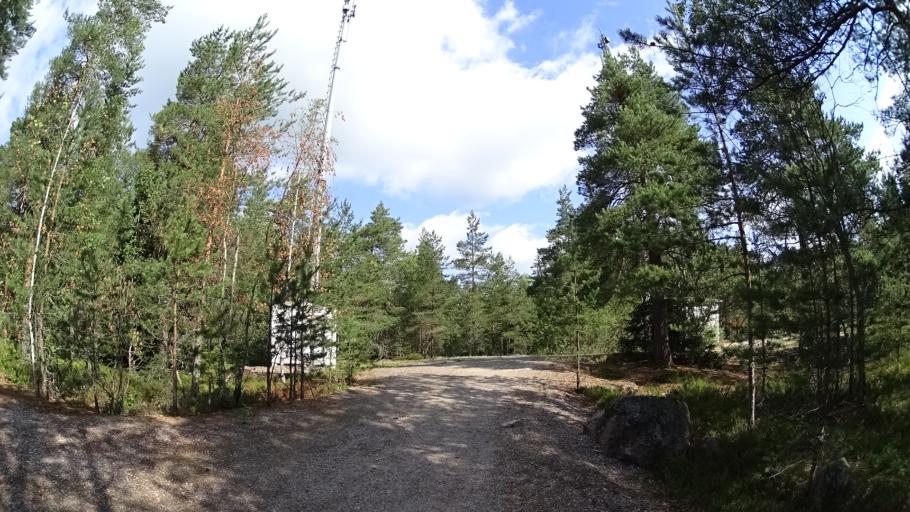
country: FI
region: Uusimaa
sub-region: Helsinki
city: Teekkarikylae
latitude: 60.2765
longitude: 24.9010
